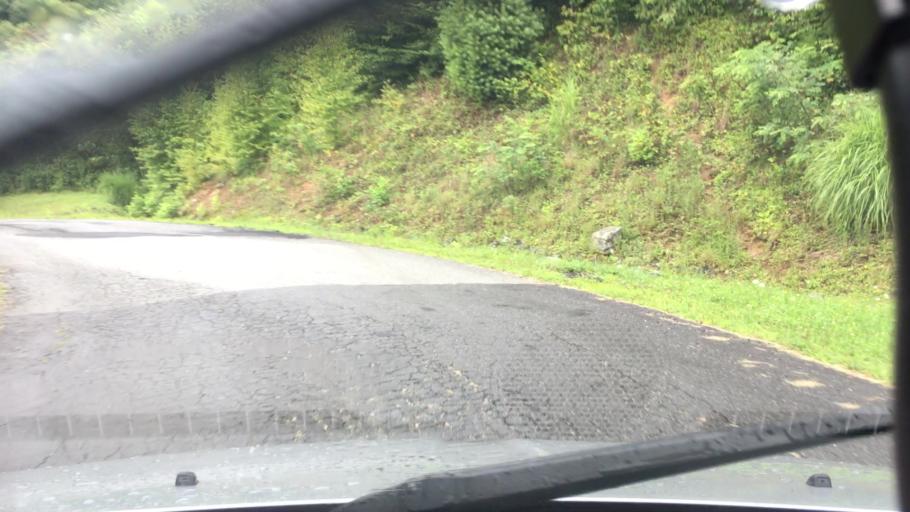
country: US
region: North Carolina
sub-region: Madison County
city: Mars Hill
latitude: 35.9492
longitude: -82.5182
